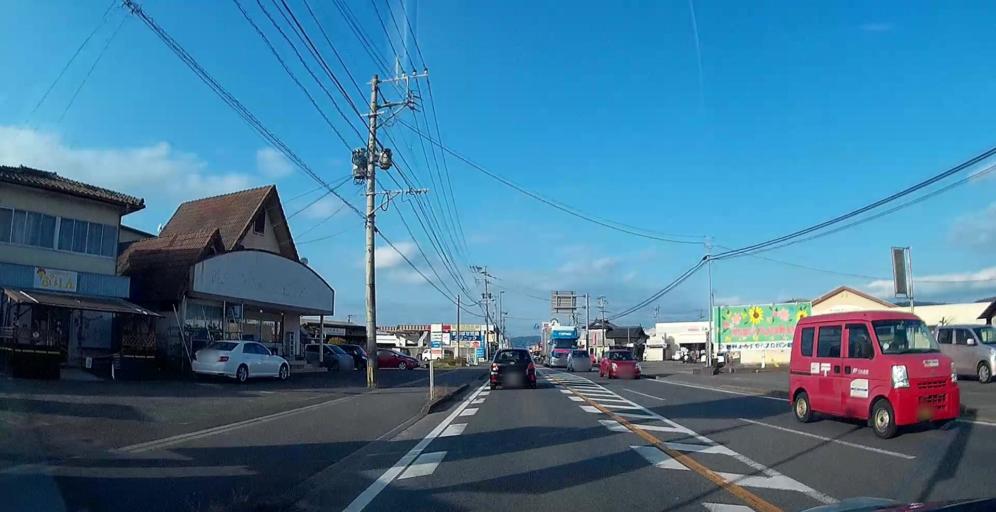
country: JP
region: Kumamoto
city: Matsubase
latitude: 32.5952
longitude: 130.7025
